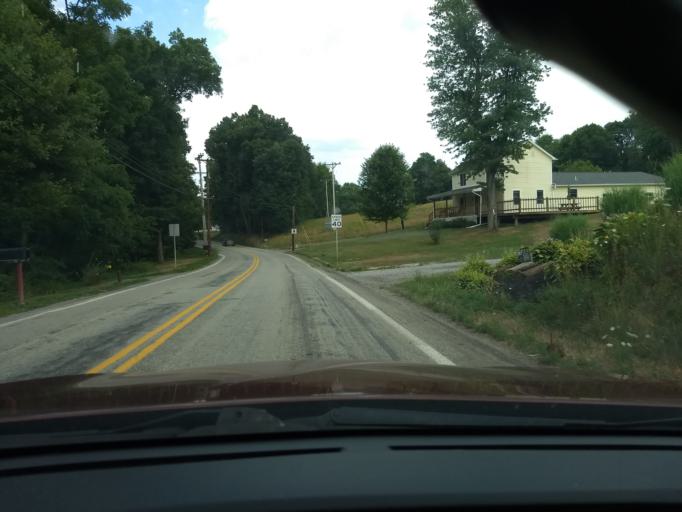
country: US
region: Pennsylvania
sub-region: Allegheny County
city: Curtisville
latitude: 40.6587
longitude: -79.8697
